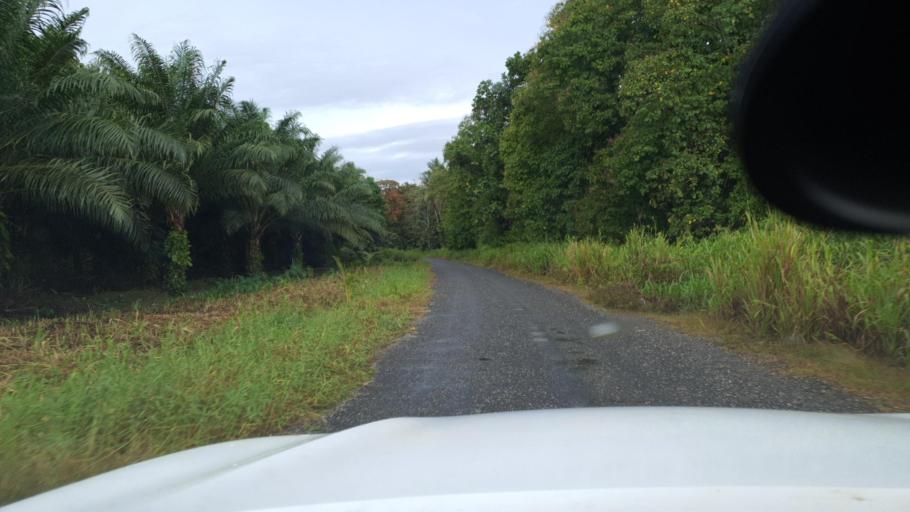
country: SB
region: Guadalcanal
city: Honiara
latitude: -9.4805
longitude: 160.3551
